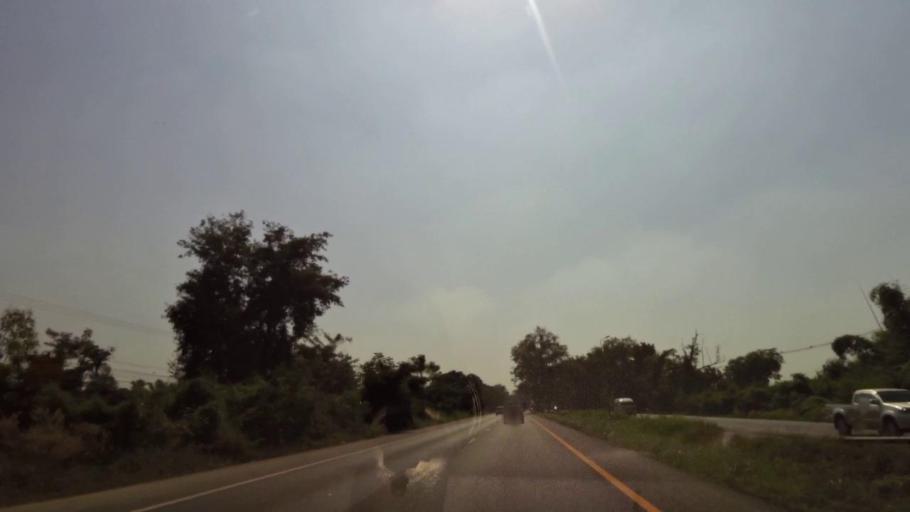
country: TH
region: Phichit
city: Bueng Na Rang
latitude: 16.0376
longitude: 100.1171
